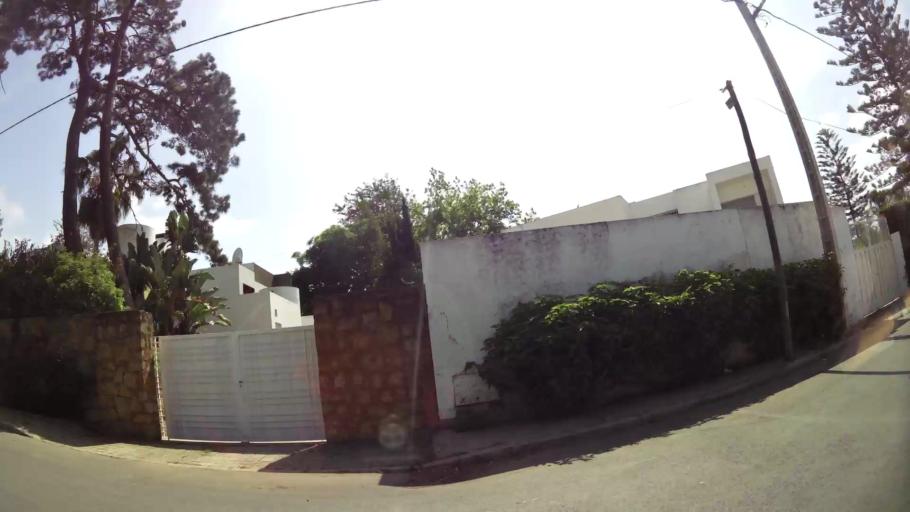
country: MA
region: Rabat-Sale-Zemmour-Zaer
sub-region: Rabat
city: Rabat
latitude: 33.9859
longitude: -6.8328
